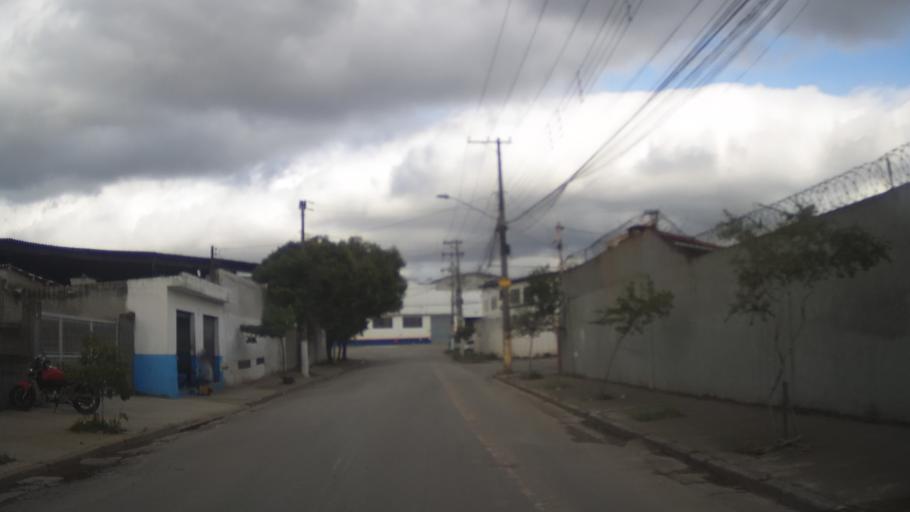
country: BR
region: Sao Paulo
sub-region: Guarulhos
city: Guarulhos
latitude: -23.4642
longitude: -46.4719
